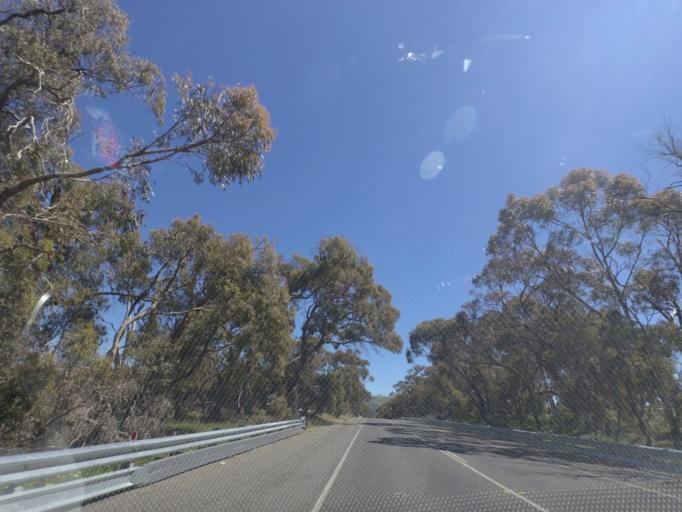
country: AU
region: Victoria
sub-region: Hume
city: Sunbury
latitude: -37.3019
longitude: 144.8291
